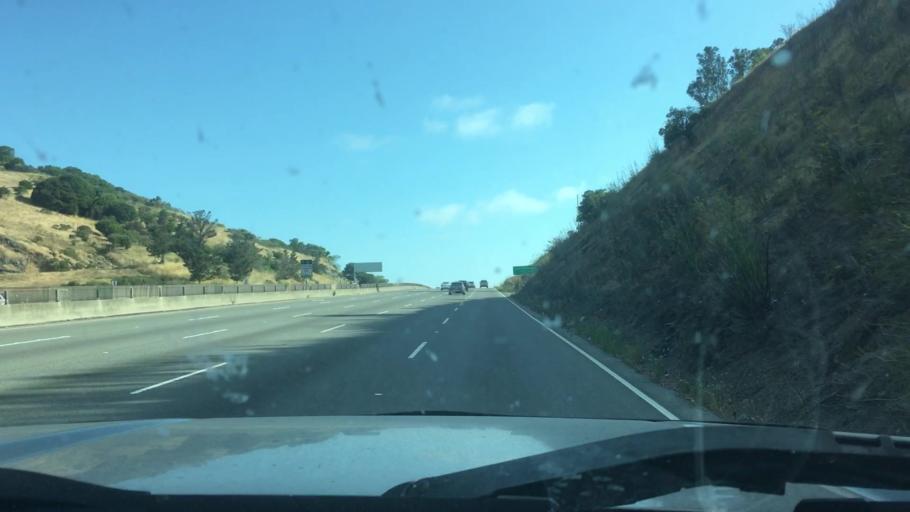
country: US
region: California
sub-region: Marin County
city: Strawberry
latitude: 37.9074
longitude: -122.5144
